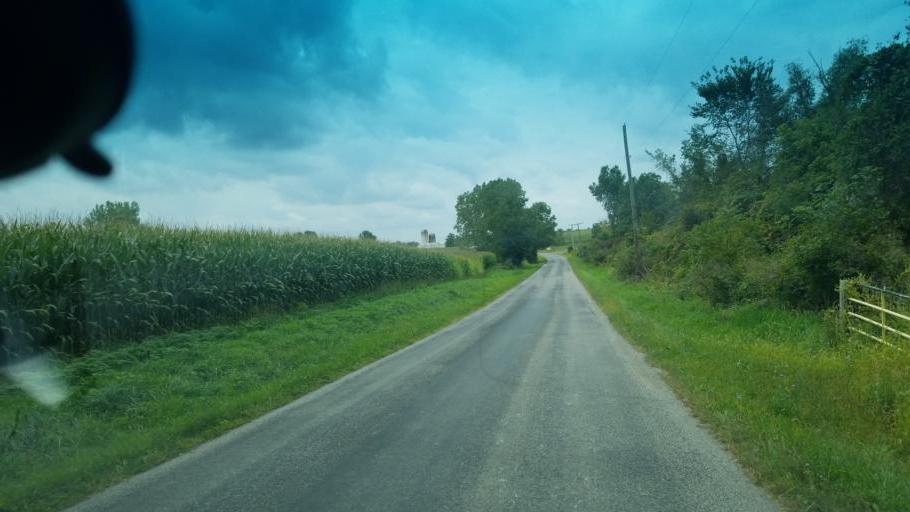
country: US
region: Ohio
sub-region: Huron County
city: Greenwich
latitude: 40.9331
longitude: -82.5491
